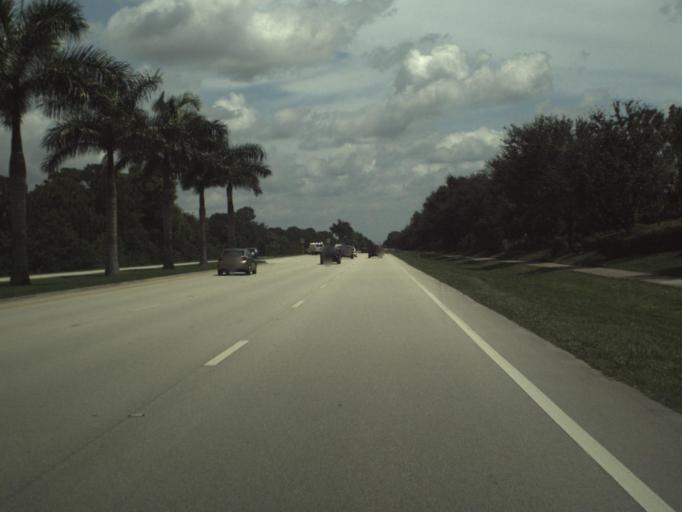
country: US
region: Florida
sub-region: Palm Beach County
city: Juno Beach
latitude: 26.8886
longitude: -80.0949
